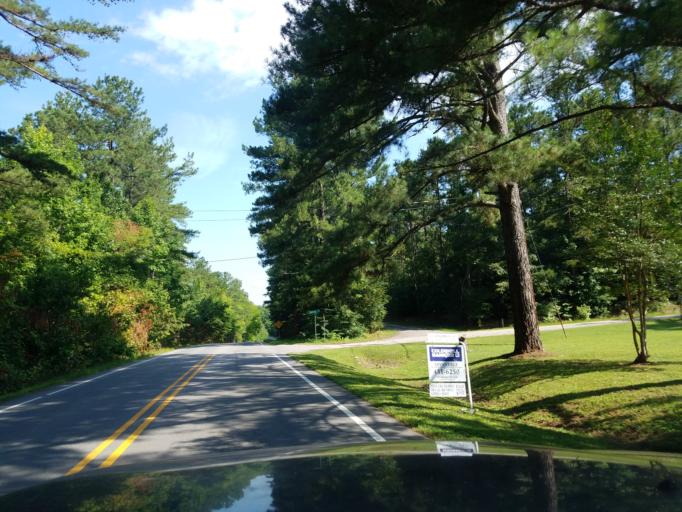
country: US
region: North Carolina
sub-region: Vance County
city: Henderson
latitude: 36.3450
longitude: -78.4133
